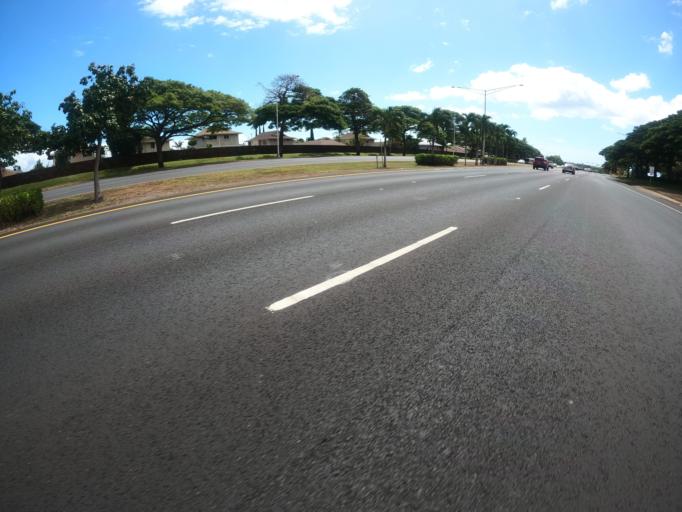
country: US
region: Hawaii
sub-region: Honolulu County
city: Royal Kunia
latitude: 21.3718
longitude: -158.0261
